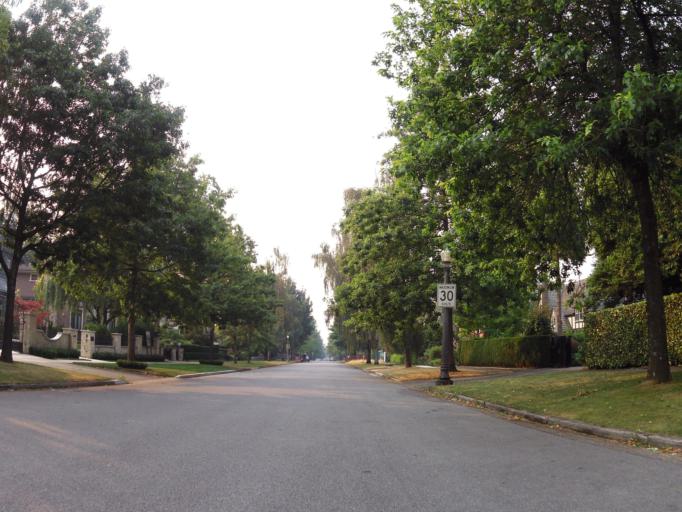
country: CA
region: British Columbia
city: Vancouver
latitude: 49.2339
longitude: -123.1477
